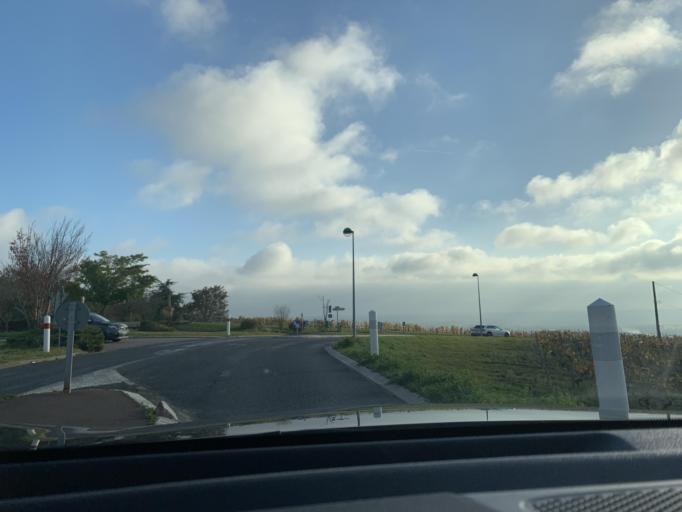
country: FR
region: Rhone-Alpes
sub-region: Departement du Rhone
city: Pommiers
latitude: 45.9510
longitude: 4.6985
